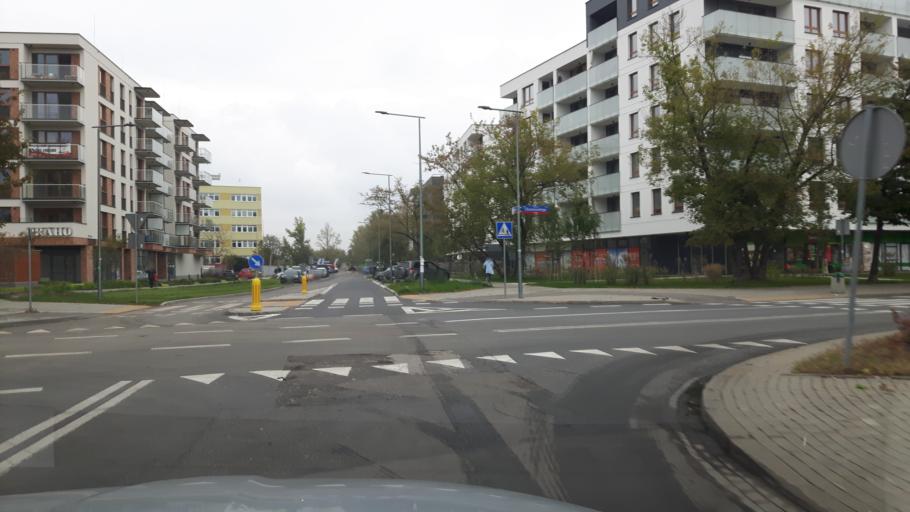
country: PL
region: Masovian Voivodeship
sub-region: Warszawa
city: Praga Poludnie
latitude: 52.2519
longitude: 21.0743
